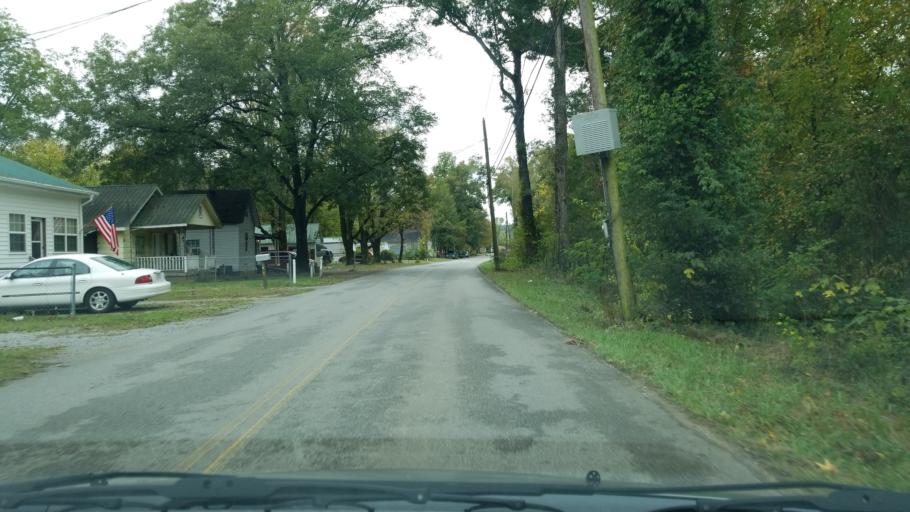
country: US
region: Tennessee
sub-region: Rhea County
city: Dayton
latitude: 35.5052
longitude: -85.0242
